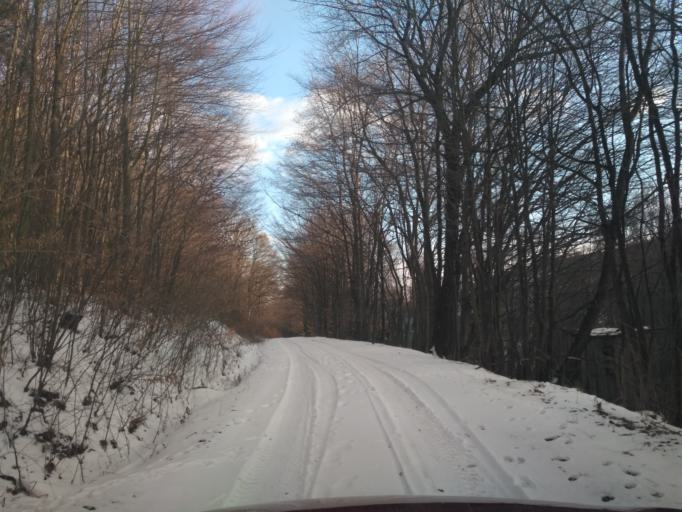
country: SK
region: Kosicky
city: Kosice
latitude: 48.7475
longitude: 21.1513
